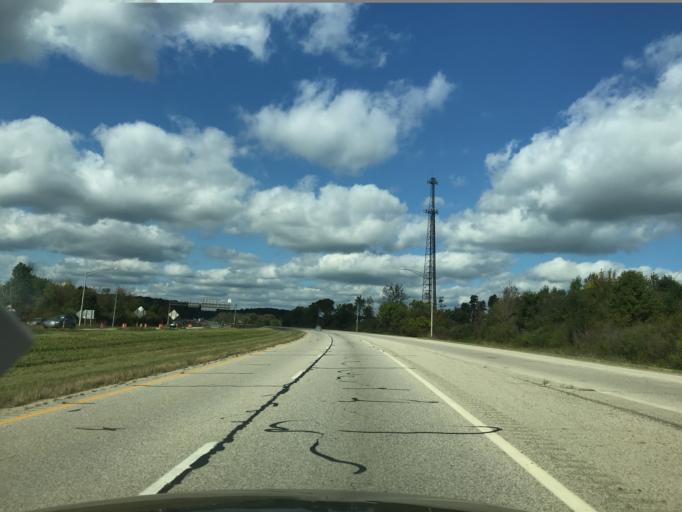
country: US
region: Ohio
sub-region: Portage County
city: Streetsboro
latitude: 41.2627
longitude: -81.3791
